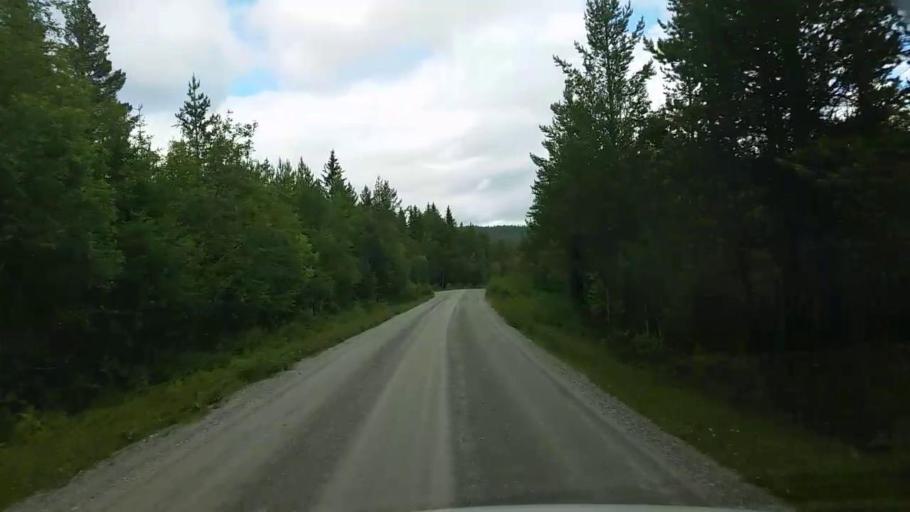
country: NO
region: Hedmark
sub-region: Engerdal
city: Engerdal
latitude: 62.4229
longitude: 12.6759
